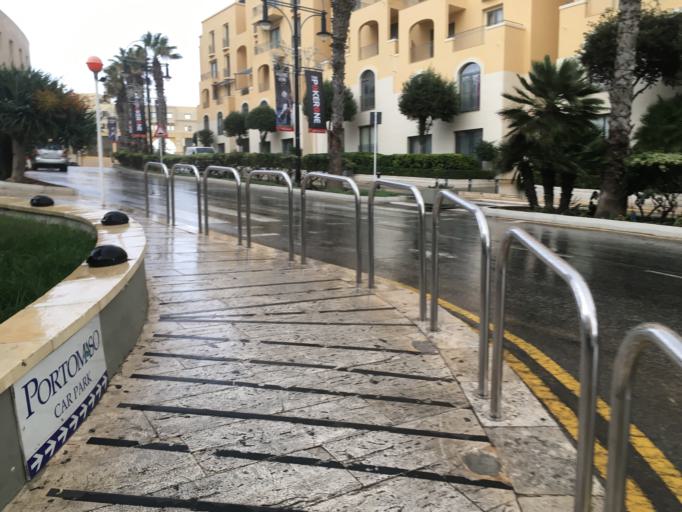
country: MT
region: Saint Julian
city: San Giljan
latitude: 35.9215
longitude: 14.4916
